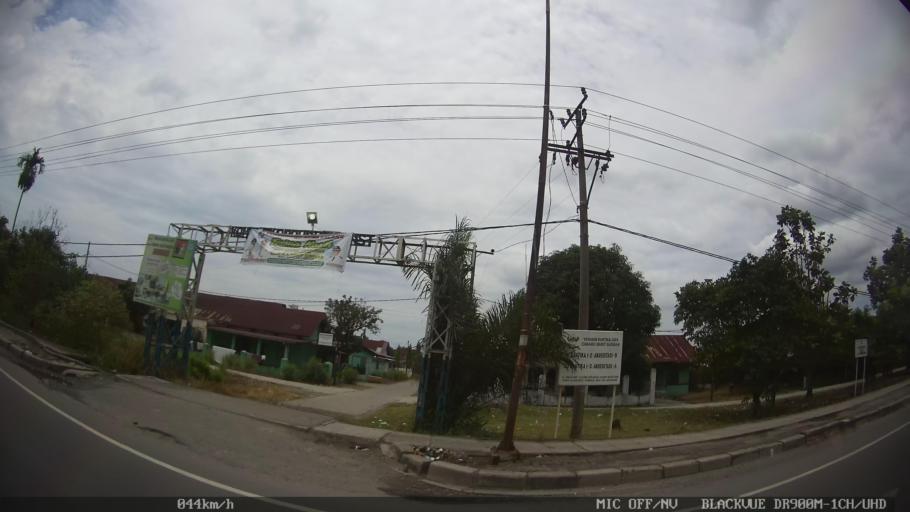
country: ID
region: North Sumatra
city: Sunggal
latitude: 3.5992
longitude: 98.5999
